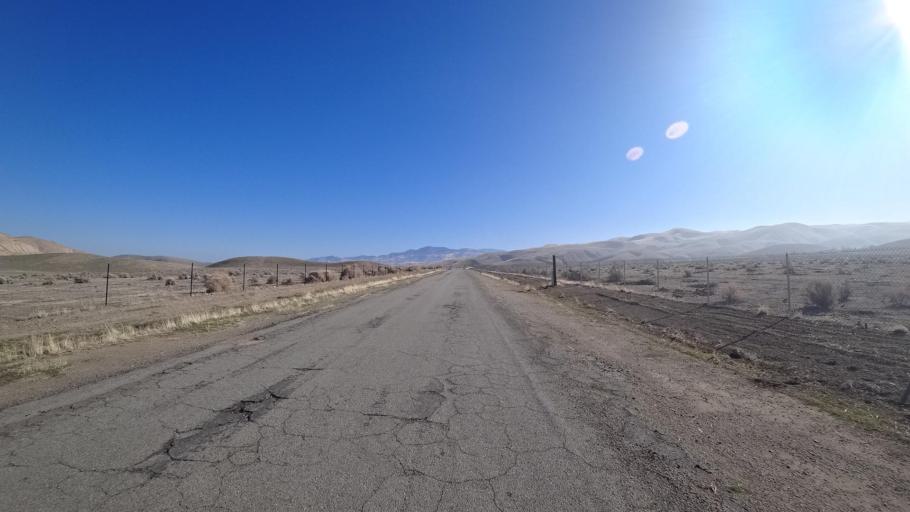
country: US
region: California
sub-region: Kern County
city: Maricopa
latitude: 34.9949
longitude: -119.3950
